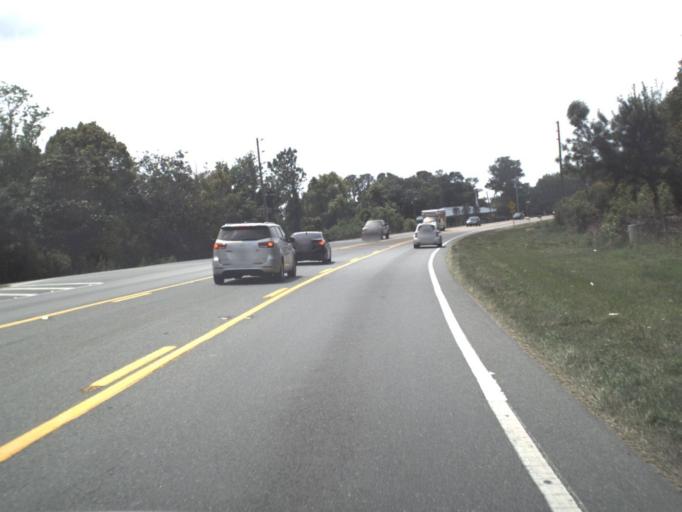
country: US
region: Florida
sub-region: Lake County
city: Mount Dora
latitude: 28.8402
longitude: -81.6342
